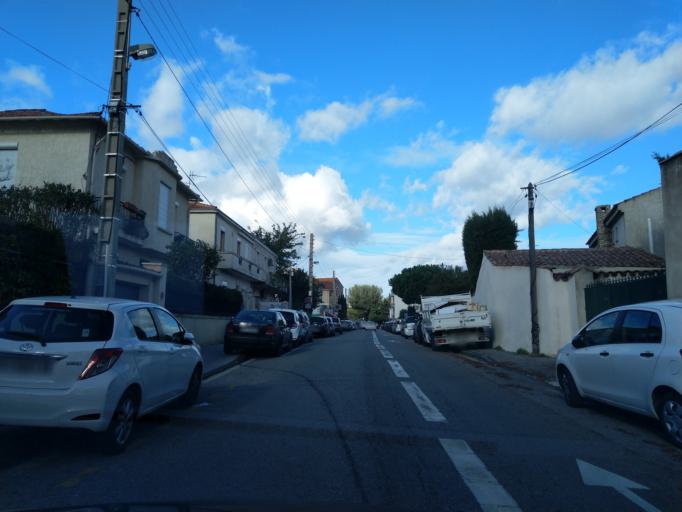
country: FR
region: Provence-Alpes-Cote d'Azur
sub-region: Departement des Bouches-du-Rhone
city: Marseille 12
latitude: 43.3071
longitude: 5.4378
